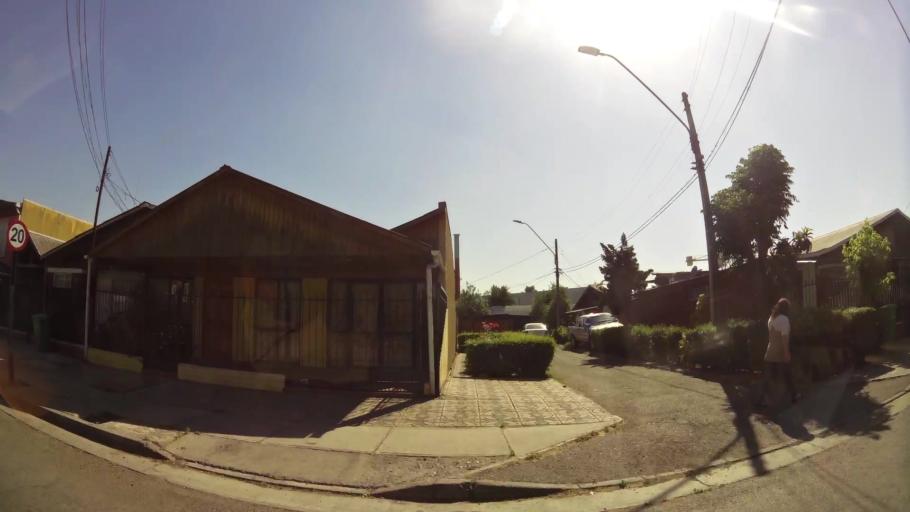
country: CL
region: Santiago Metropolitan
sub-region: Provincia de Maipo
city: San Bernardo
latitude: -33.5577
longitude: -70.7075
